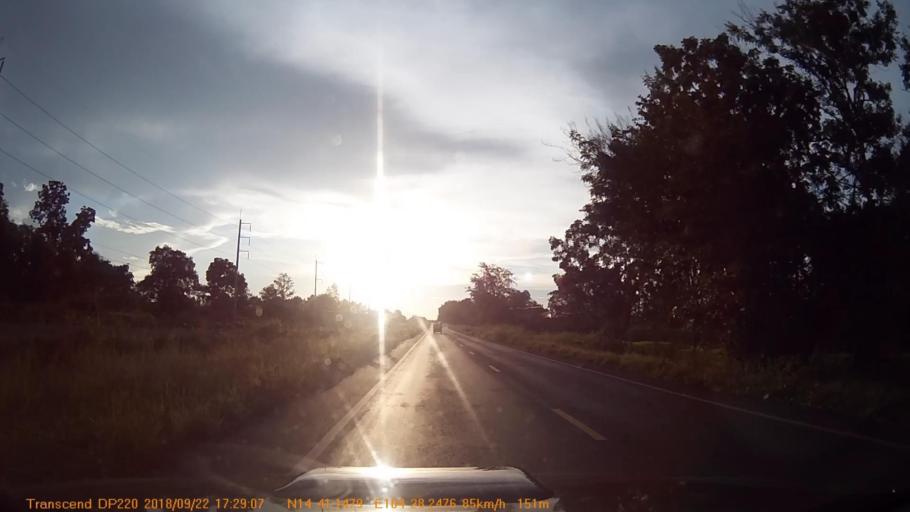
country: TH
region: Sisaket
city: Khun Han
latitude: 14.6858
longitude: 104.4703
